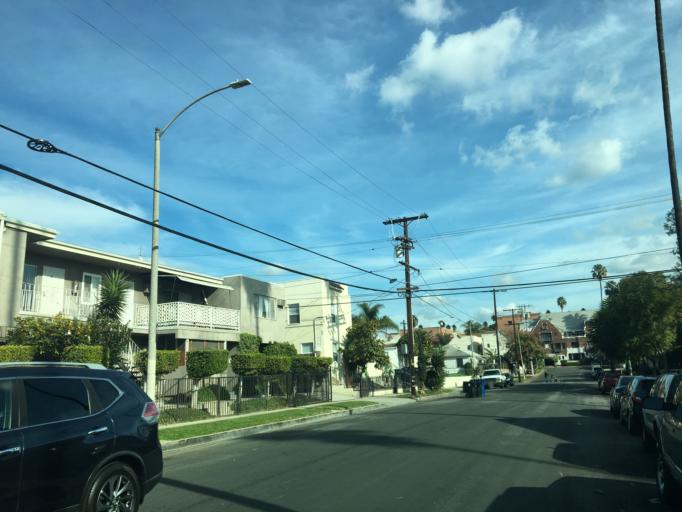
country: US
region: California
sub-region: Los Angeles County
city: Silver Lake
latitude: 34.0752
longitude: -118.2992
